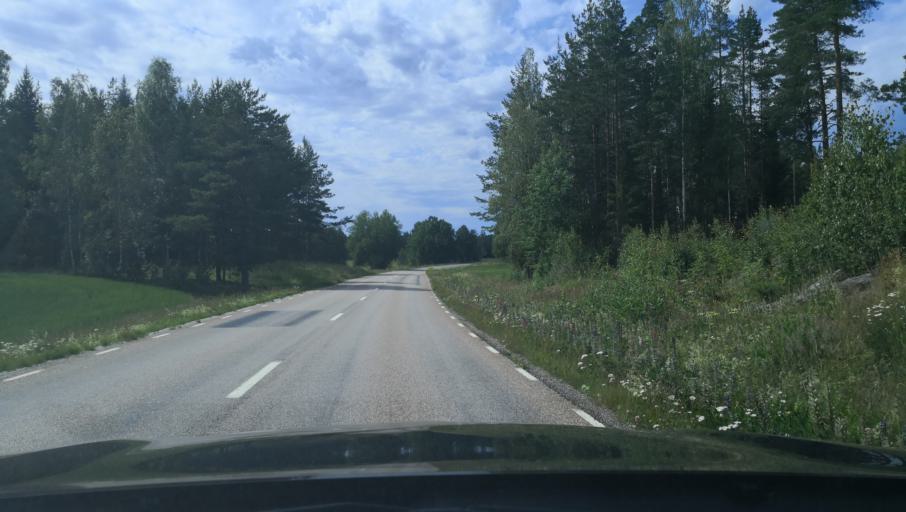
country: SE
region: Dalarna
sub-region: Avesta Kommun
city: Avesta
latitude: 59.9819
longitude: 16.1276
